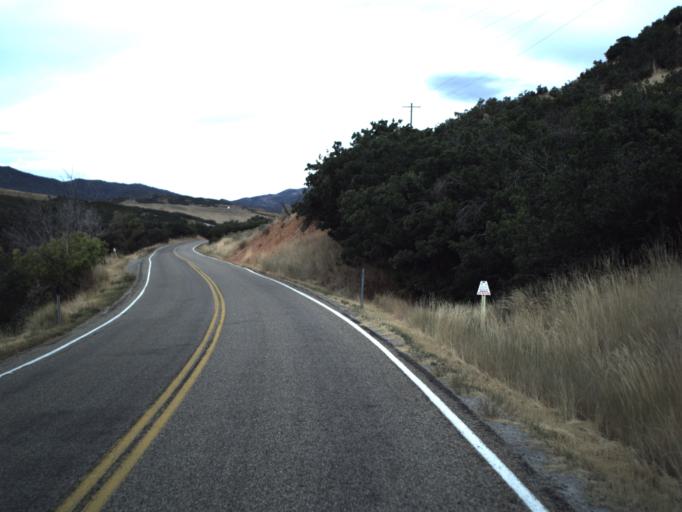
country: US
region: Utah
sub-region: Morgan County
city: Morgan
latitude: 40.9440
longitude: -111.6477
